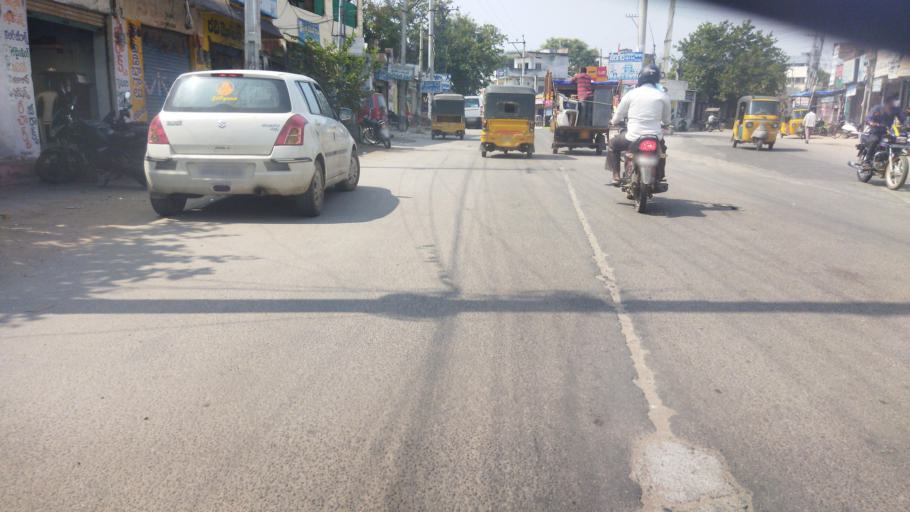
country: IN
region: Telangana
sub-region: Nalgonda
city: Nalgonda
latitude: 17.0636
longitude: 79.2774
